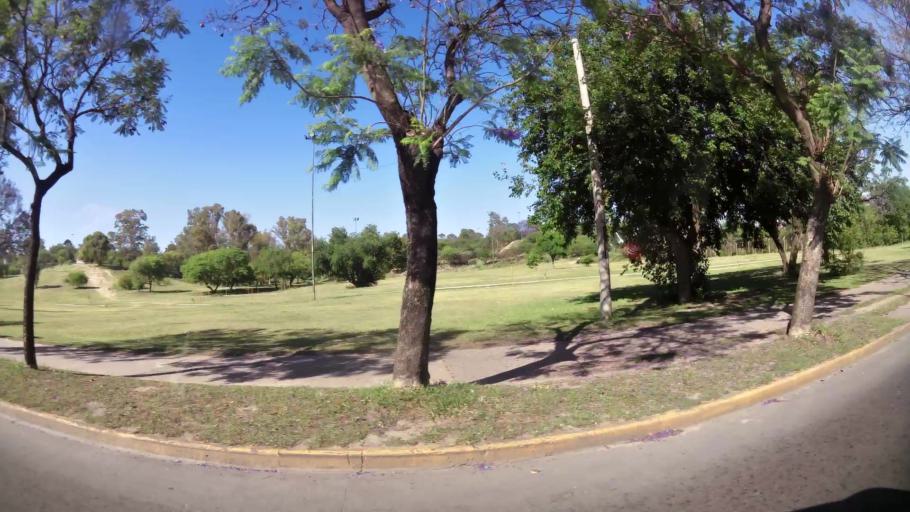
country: AR
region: Cordoba
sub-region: Departamento de Capital
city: Cordoba
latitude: -31.4279
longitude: -64.1716
